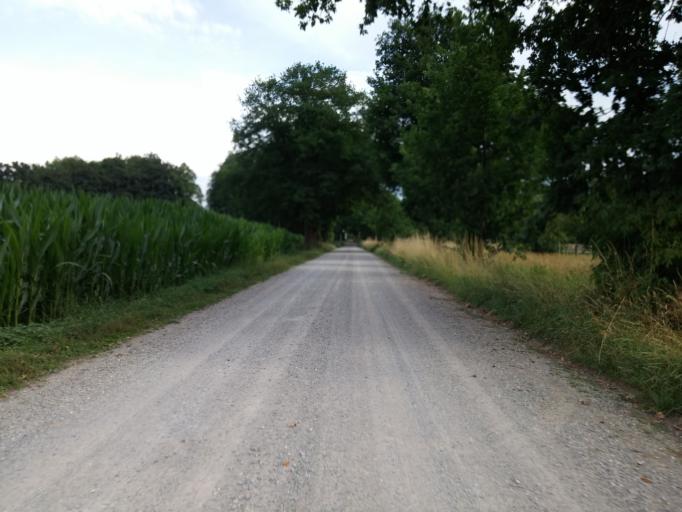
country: DE
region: North Rhine-Westphalia
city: Tonisvorst
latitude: 51.3854
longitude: 6.5262
